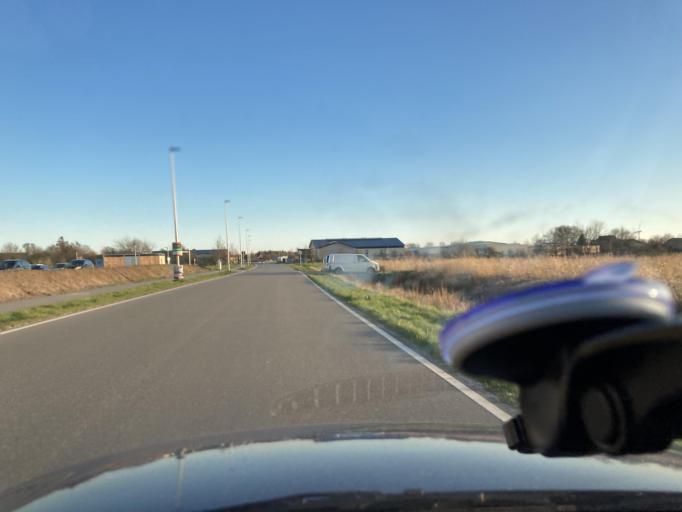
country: DE
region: Schleswig-Holstein
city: Lohe-Rickelshof
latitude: 54.1969
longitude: 9.0732
